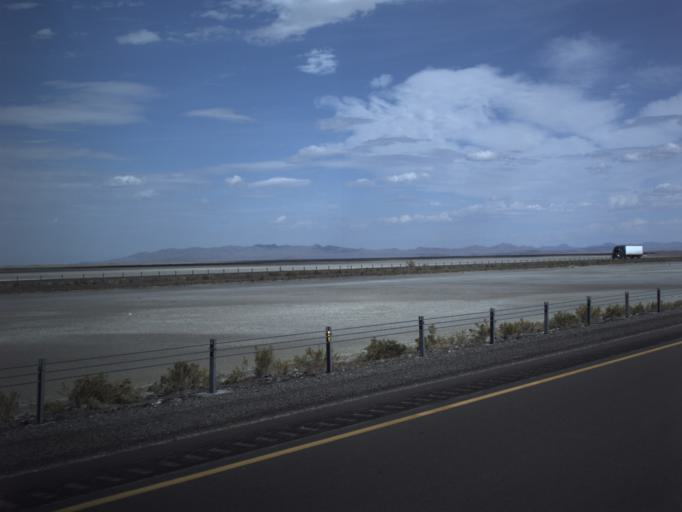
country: US
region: Utah
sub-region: Tooele County
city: Wendover
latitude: 40.7280
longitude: -113.3717
